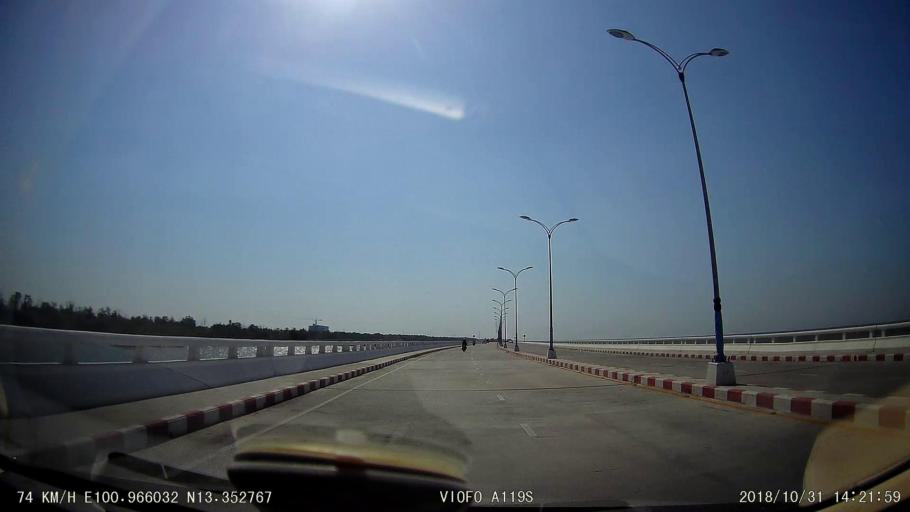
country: TH
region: Chon Buri
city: Chon Buri
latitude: 13.3527
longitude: 100.9657
